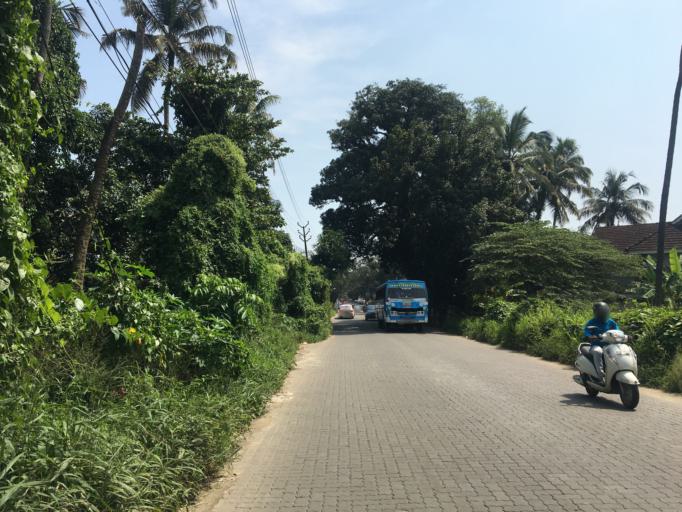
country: IN
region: Kerala
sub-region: Ernakulam
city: Cochin
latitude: 9.9623
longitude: 76.3200
